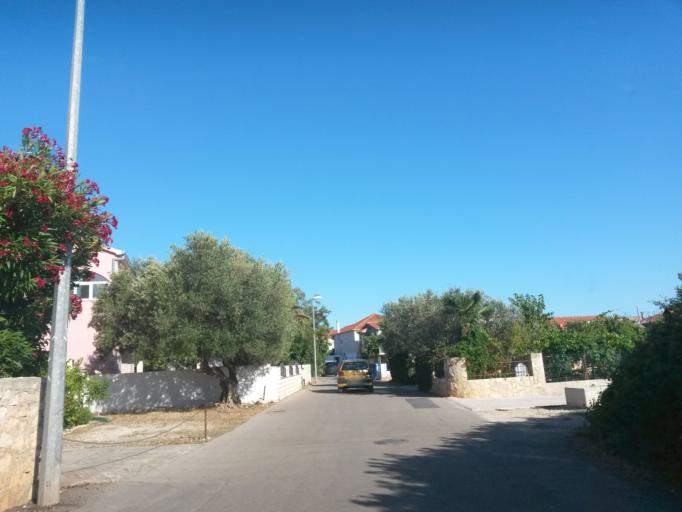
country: HR
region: Sibensko-Kniniska
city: Rogoznica
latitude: 43.5359
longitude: 15.9634
